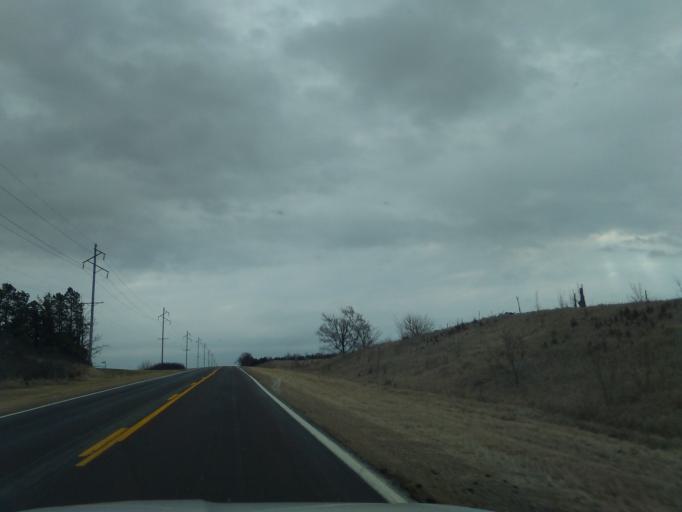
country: US
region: Nebraska
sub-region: Nemaha County
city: Auburn
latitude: 40.4797
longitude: -95.9889
